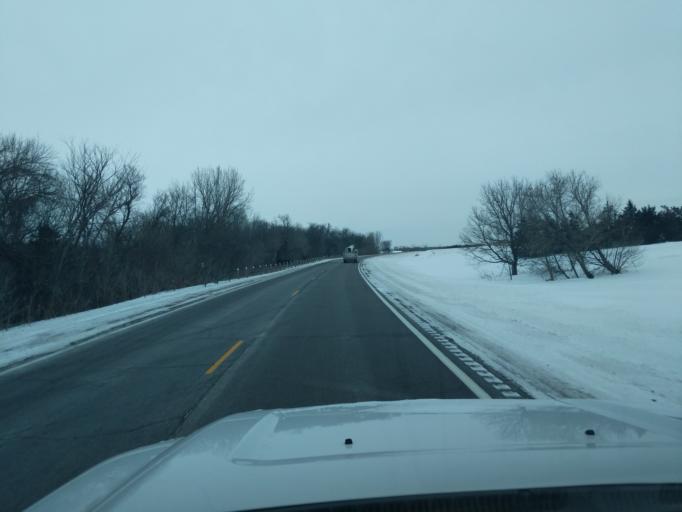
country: US
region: Minnesota
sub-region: Redwood County
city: Redwood Falls
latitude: 44.5679
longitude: -94.9949
